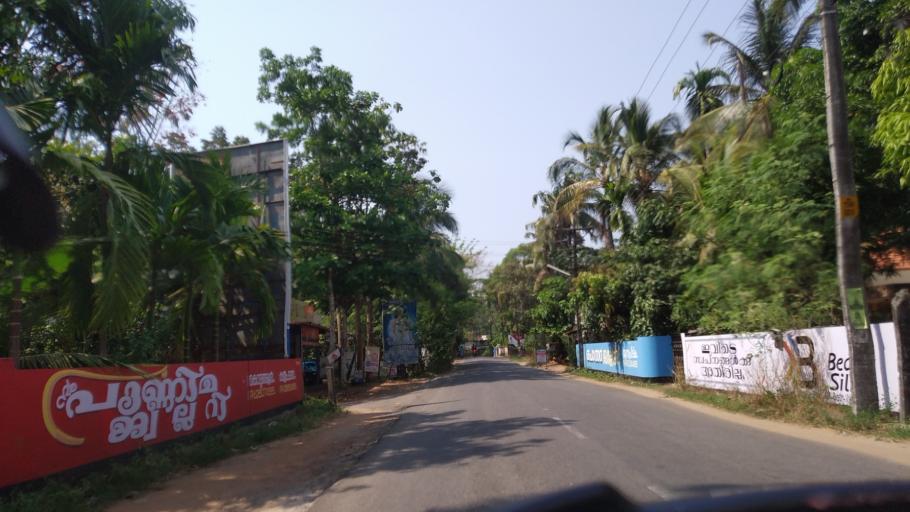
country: IN
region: Kerala
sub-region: Thrissur District
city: Kodungallur
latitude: 10.2734
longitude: 76.1396
